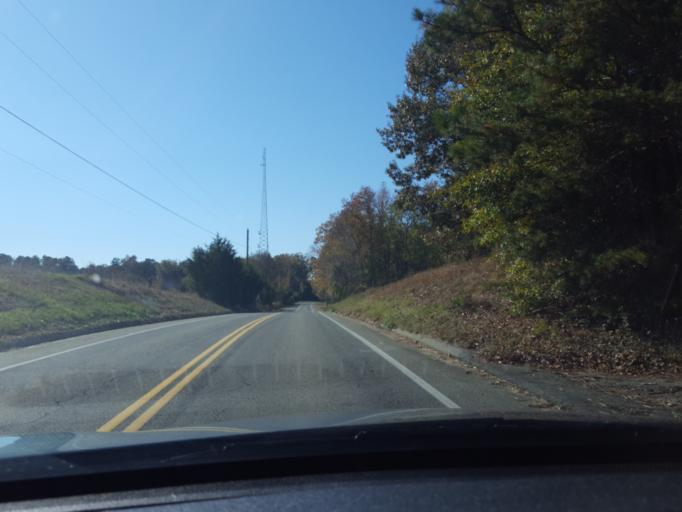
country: US
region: Maryland
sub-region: Saint Mary's County
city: Leonardtown
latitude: 38.2730
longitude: -76.6012
